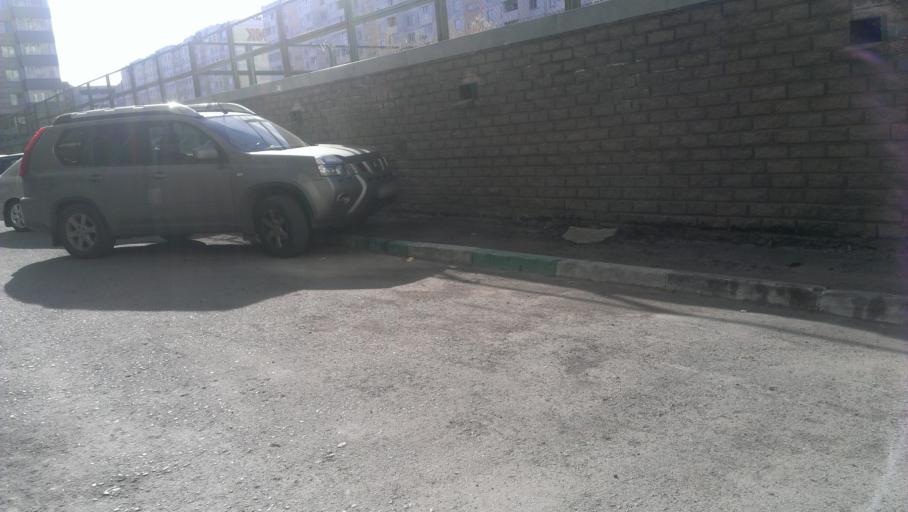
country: RU
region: Altai Krai
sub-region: Gorod Barnaulskiy
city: Barnaul
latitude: 53.3379
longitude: 83.6932
